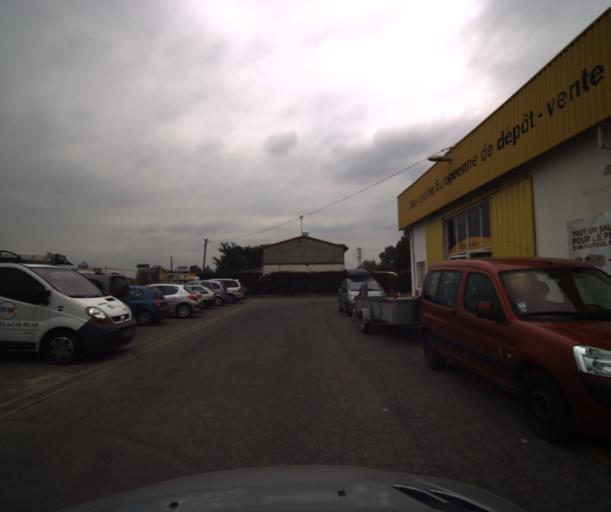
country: FR
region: Midi-Pyrenees
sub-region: Departement de la Haute-Garonne
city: Portet-sur-Garonne
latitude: 43.5366
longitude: 1.3984
